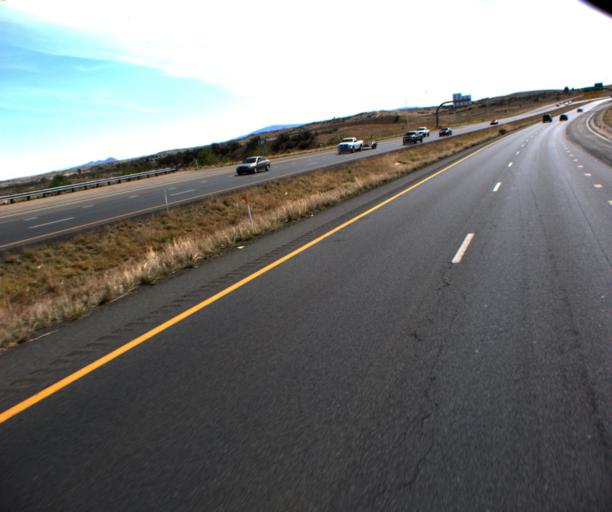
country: US
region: Arizona
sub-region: Yavapai County
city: Prescott Valley
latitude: 34.6370
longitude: -112.4090
